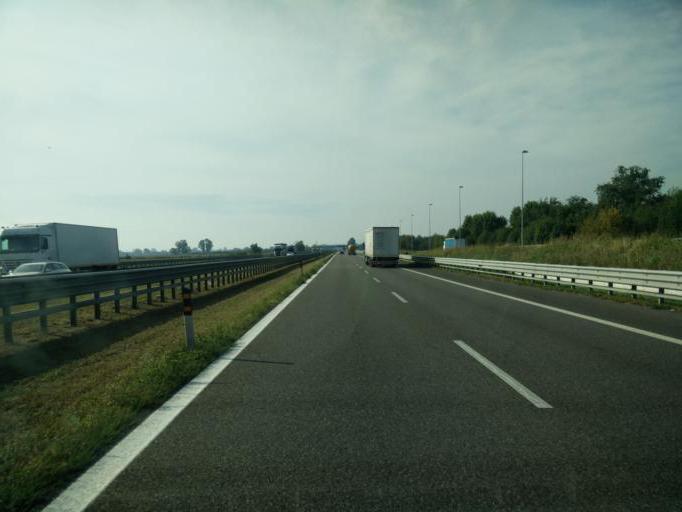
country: IT
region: Lombardy
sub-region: Provincia di Cremona
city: San Felice
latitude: 45.1314
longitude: 10.0675
